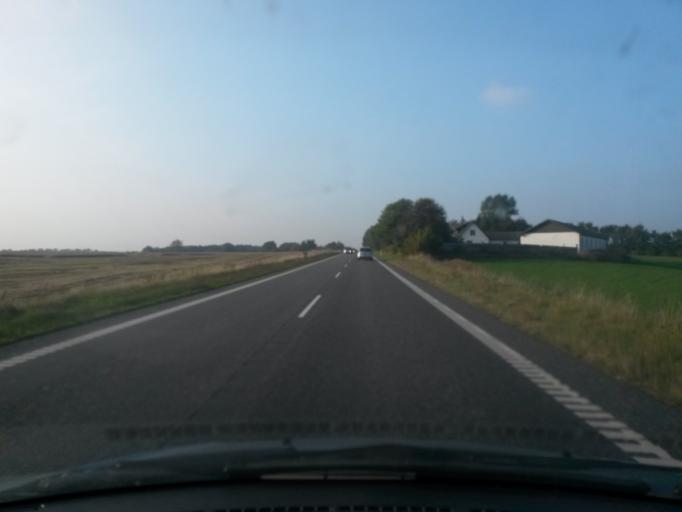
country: DK
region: Central Jutland
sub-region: Randers Kommune
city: Assentoft
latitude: 56.4331
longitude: 10.1903
